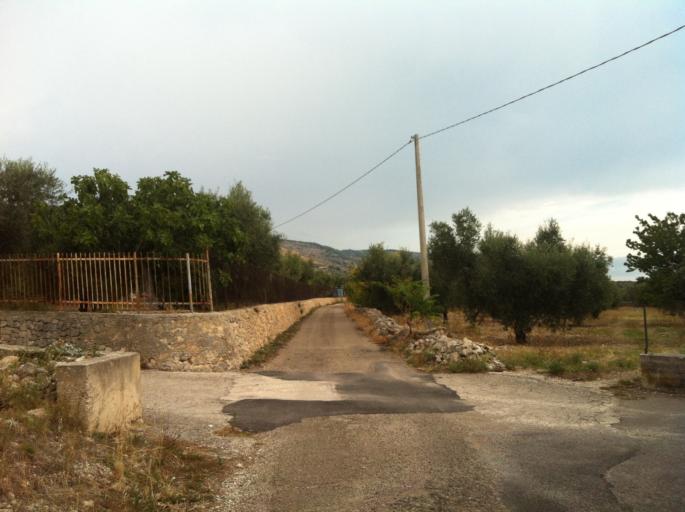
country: IT
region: Apulia
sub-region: Provincia di Foggia
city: Monte Sant'Angelo
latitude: 41.6658
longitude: 15.9518
